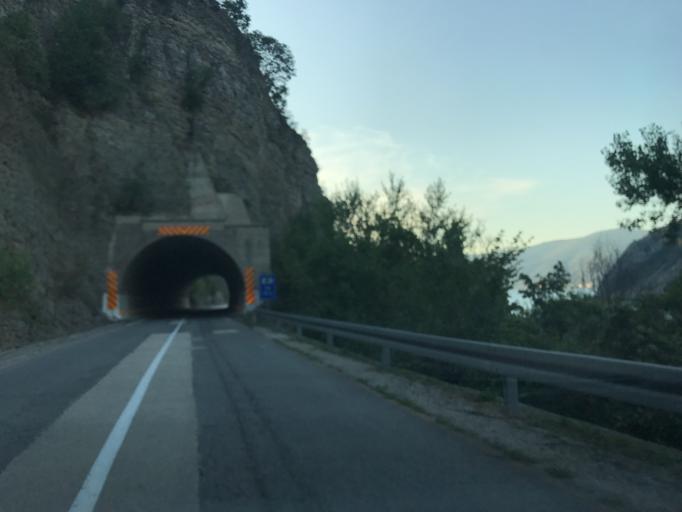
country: RO
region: Caras-Severin
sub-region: Comuna Berzasca
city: Berzasca
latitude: 44.6014
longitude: 22.0075
